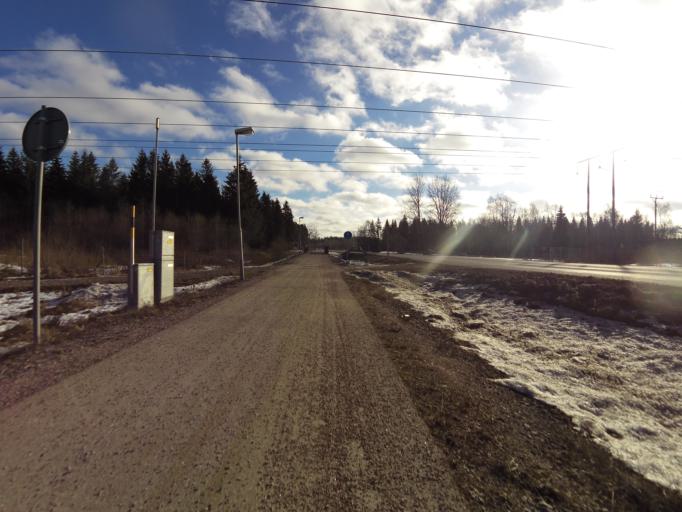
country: SE
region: Gaevleborg
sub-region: Gavle Kommun
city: Gavle
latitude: 60.6471
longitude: 17.2542
